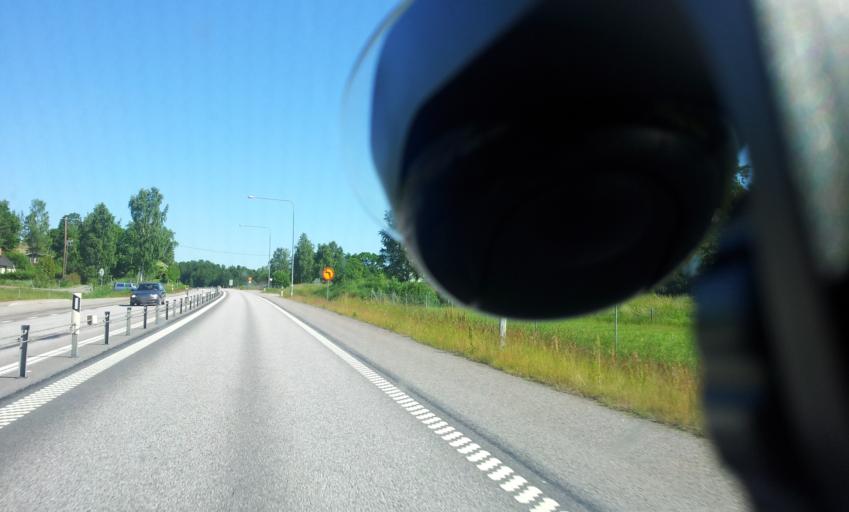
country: SE
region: OEstergoetland
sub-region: Soderkopings Kommun
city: Soederkoeping
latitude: 58.4087
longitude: 16.4019
